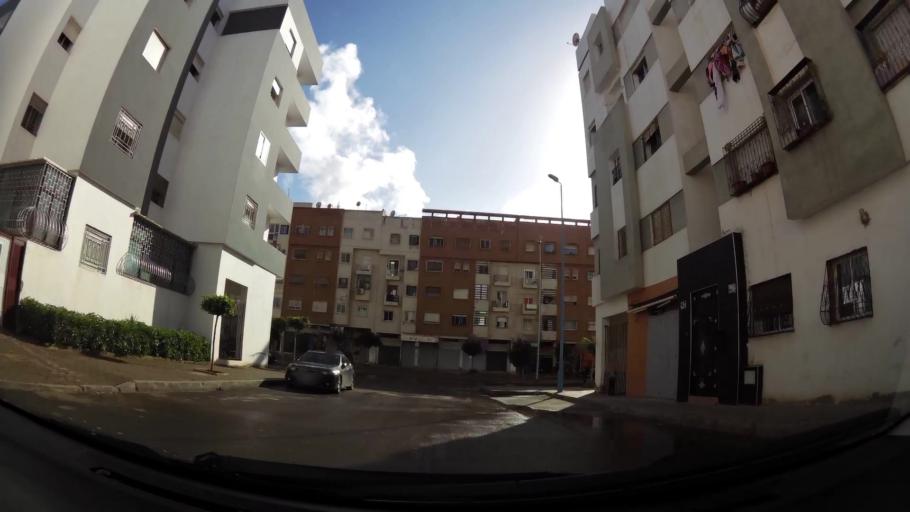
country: MA
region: Grand Casablanca
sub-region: Casablanca
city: Casablanca
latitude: 33.5575
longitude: -7.7033
